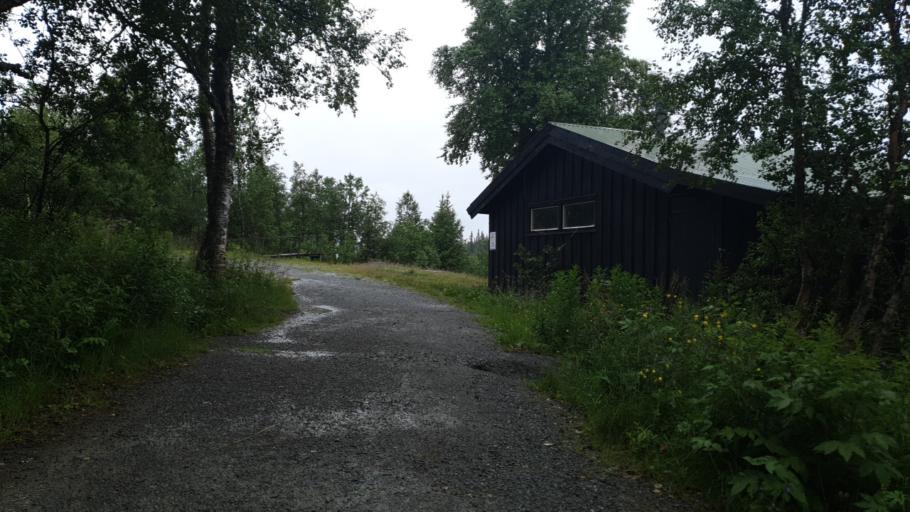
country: NO
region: Oppland
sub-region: Vestre Slidre
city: Slidre
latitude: 61.2303
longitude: 8.9252
